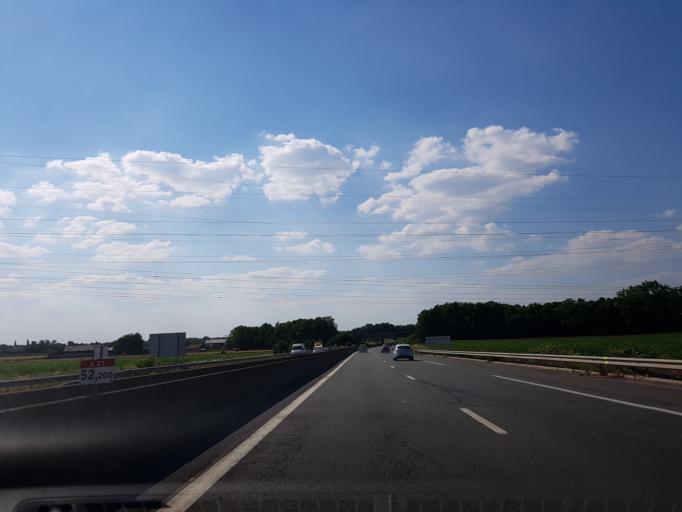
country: FR
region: Nord-Pas-de-Calais
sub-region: Departement du Nord
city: Escaudain
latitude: 50.3319
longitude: 3.3271
